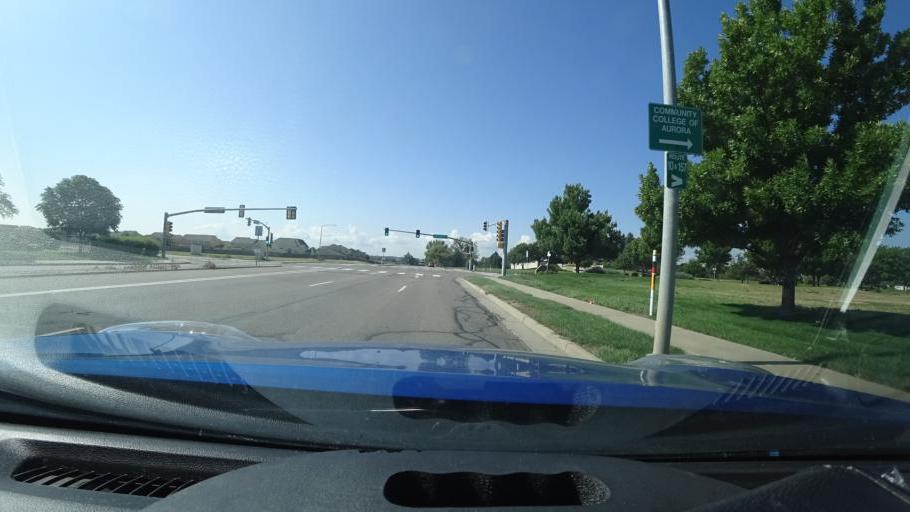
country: US
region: Colorado
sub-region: Adams County
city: Aurora
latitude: 39.7172
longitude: -104.7913
